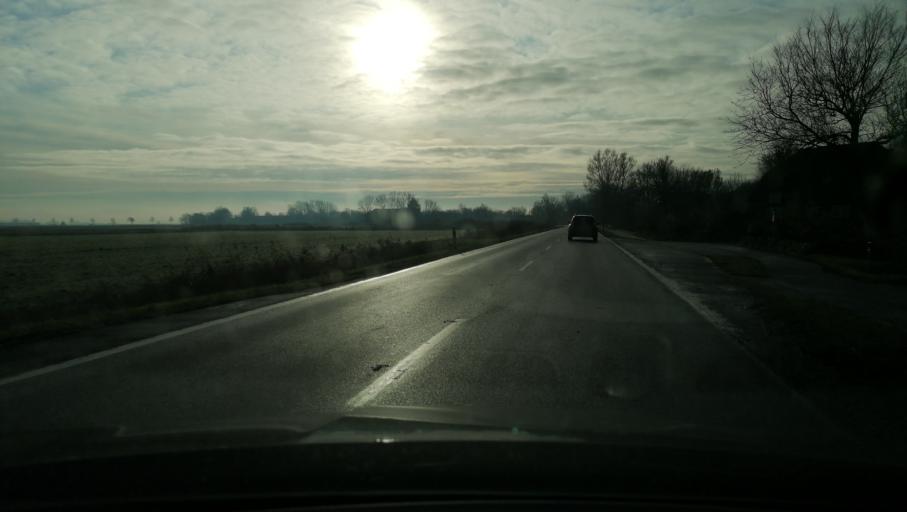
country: DE
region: Schleswig-Holstein
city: Epenwohrden
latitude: 54.1206
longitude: 9.0165
